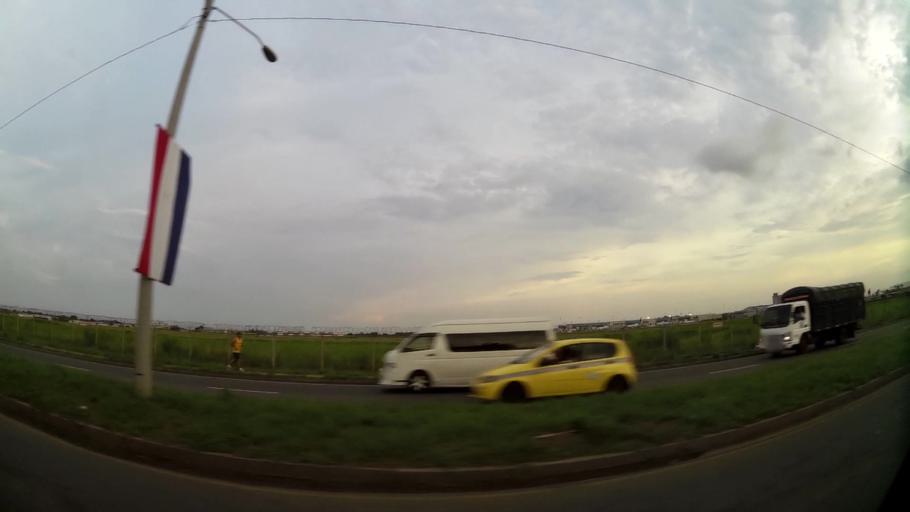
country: PA
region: Panama
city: Tocumen
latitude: 9.0751
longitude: -79.3883
